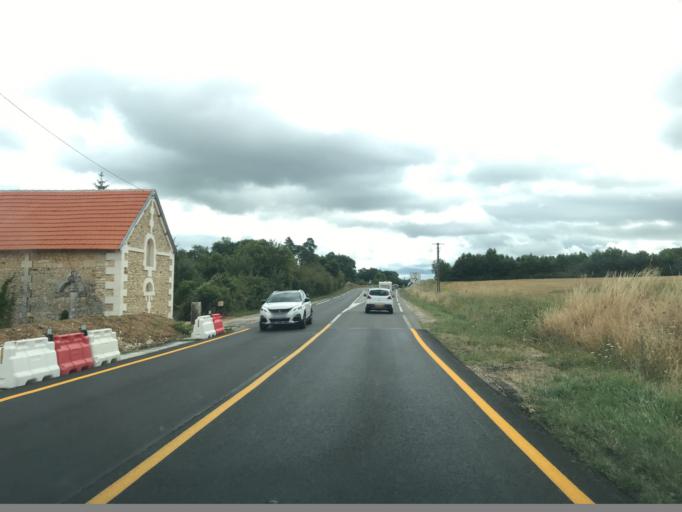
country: FR
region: Poitou-Charentes
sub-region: Departement de la Charente
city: Dignac
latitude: 45.4901
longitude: 0.3591
